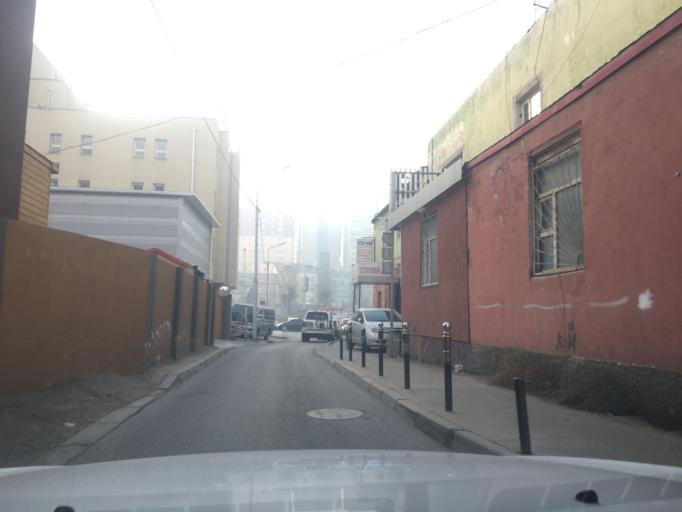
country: MN
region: Ulaanbaatar
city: Ulaanbaatar
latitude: 47.9147
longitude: 106.8656
